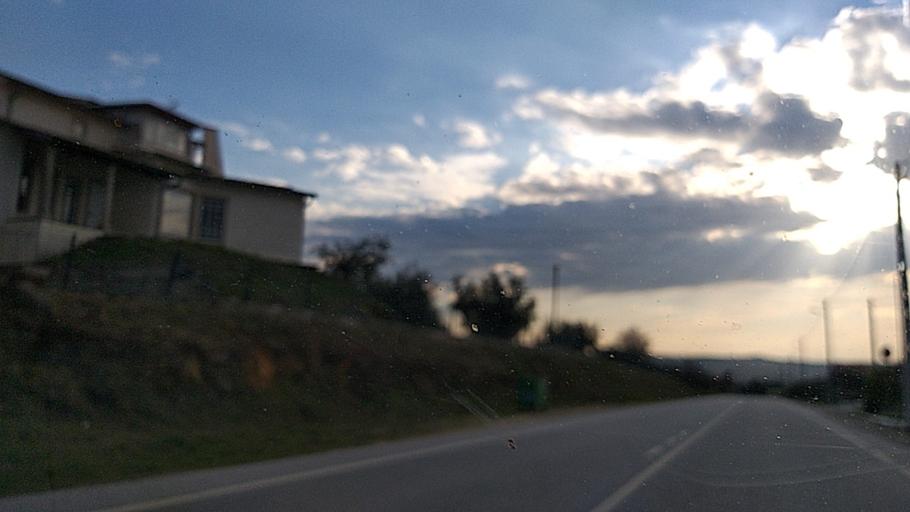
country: ES
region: Castille and Leon
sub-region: Provincia de Salamanca
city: Aldea del Obispo
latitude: 40.7141
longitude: -6.9096
